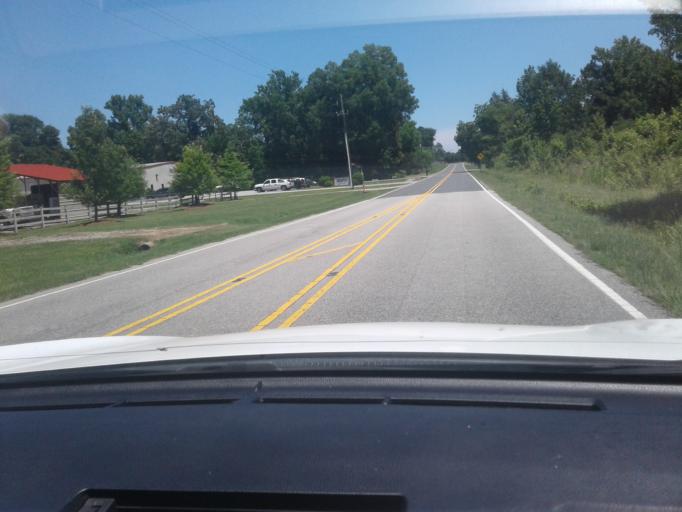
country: US
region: North Carolina
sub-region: Harnett County
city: Lillington
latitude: 35.3900
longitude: -78.7980
